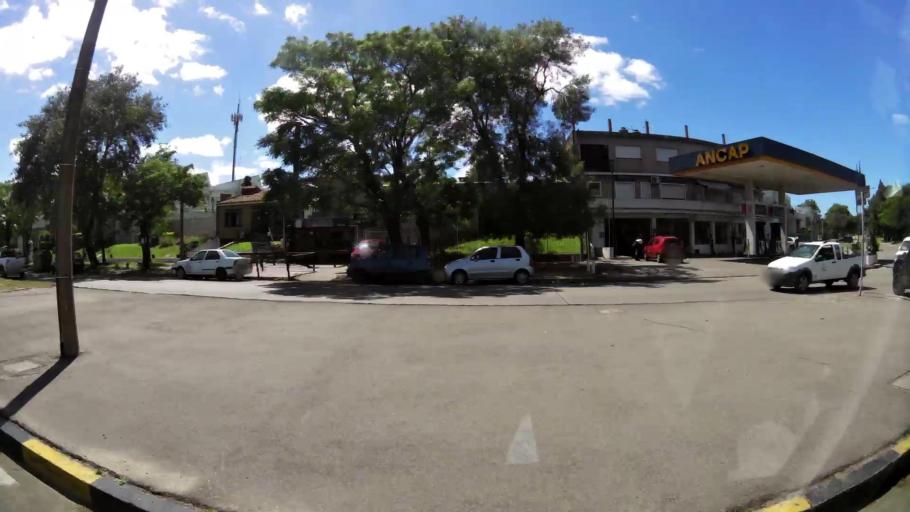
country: UY
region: Montevideo
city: Montevideo
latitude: -34.8618
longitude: -56.1516
